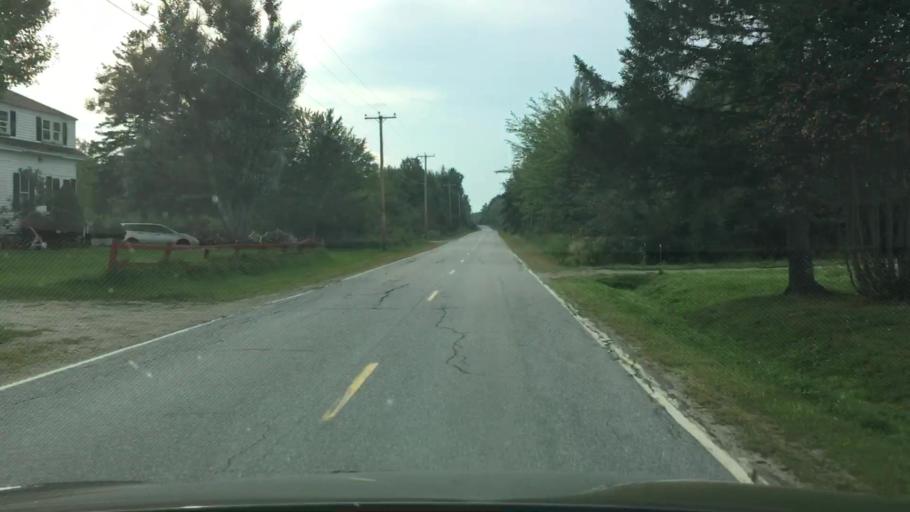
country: US
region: Maine
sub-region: Hancock County
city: Penobscot
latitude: 44.4708
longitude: -68.7468
